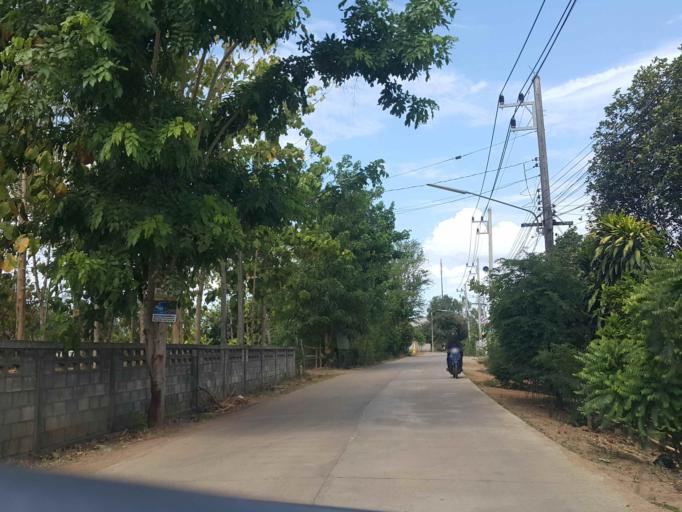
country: TH
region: Sukhothai
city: Thung Saliam
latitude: 17.3282
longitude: 99.5634
